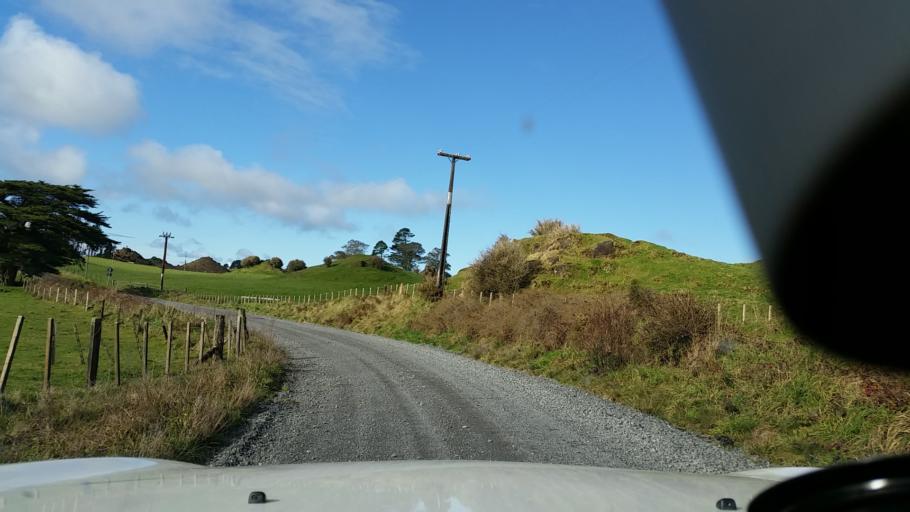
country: NZ
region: Bay of Plenty
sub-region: Rotorua District
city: Rotorua
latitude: -38.0828
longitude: 176.0539
